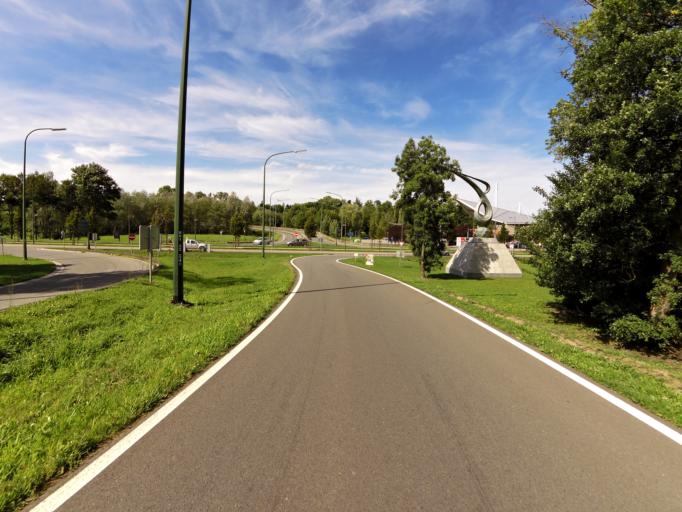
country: BE
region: Wallonia
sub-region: Province du Luxembourg
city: Marche-en-Famenne
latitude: 50.2252
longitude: 5.3390
